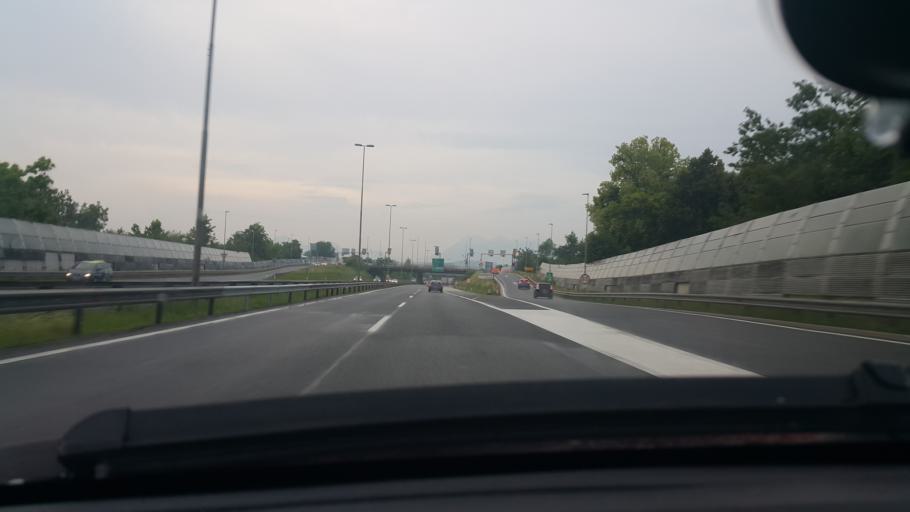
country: SI
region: Dol pri Ljubljani
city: Dol pri Ljubljani
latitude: 46.0521
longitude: 14.5743
